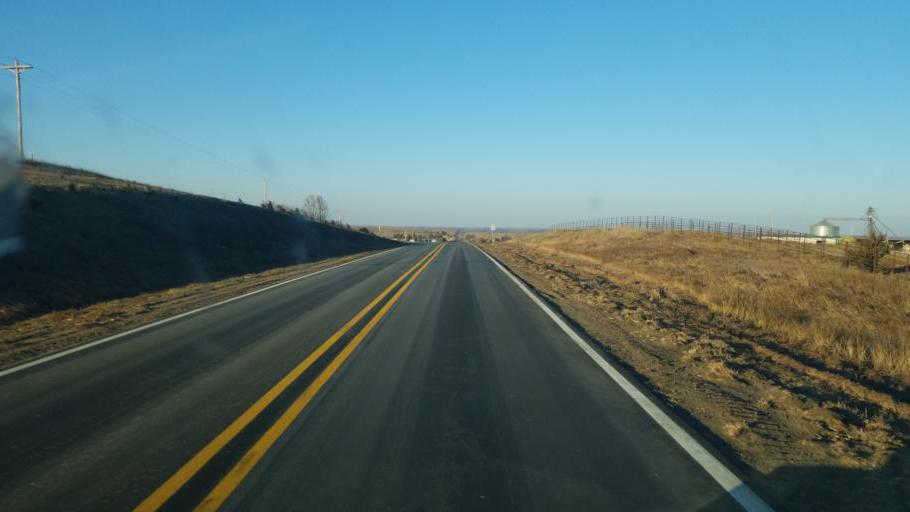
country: US
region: Nebraska
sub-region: Knox County
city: Center
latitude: 42.5971
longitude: -97.7942
